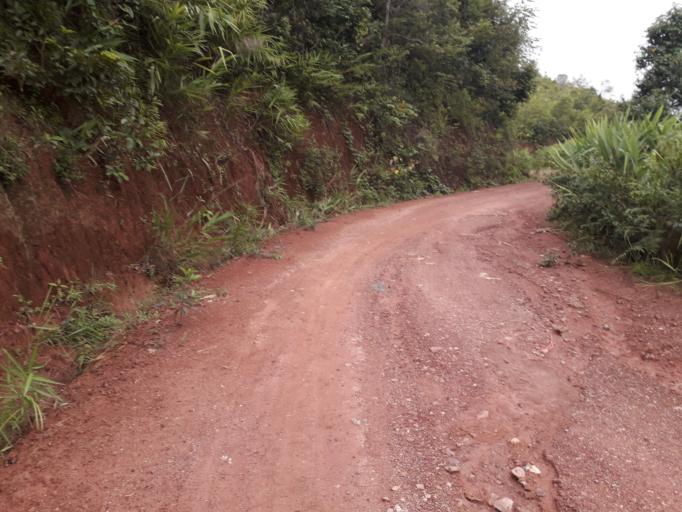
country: CN
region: Yunnan
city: Menglie
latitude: 22.2641
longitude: 101.5801
